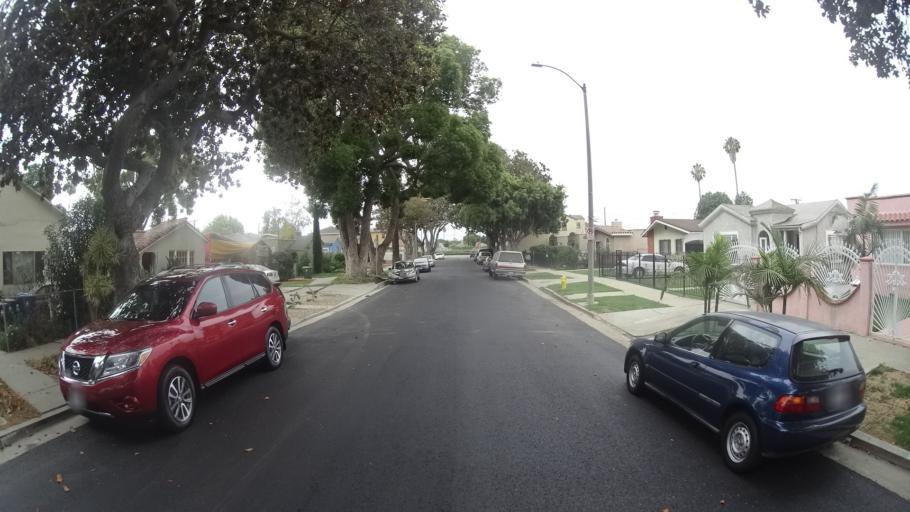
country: US
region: California
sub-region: Los Angeles County
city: View Park-Windsor Hills
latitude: 34.0248
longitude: -118.3417
